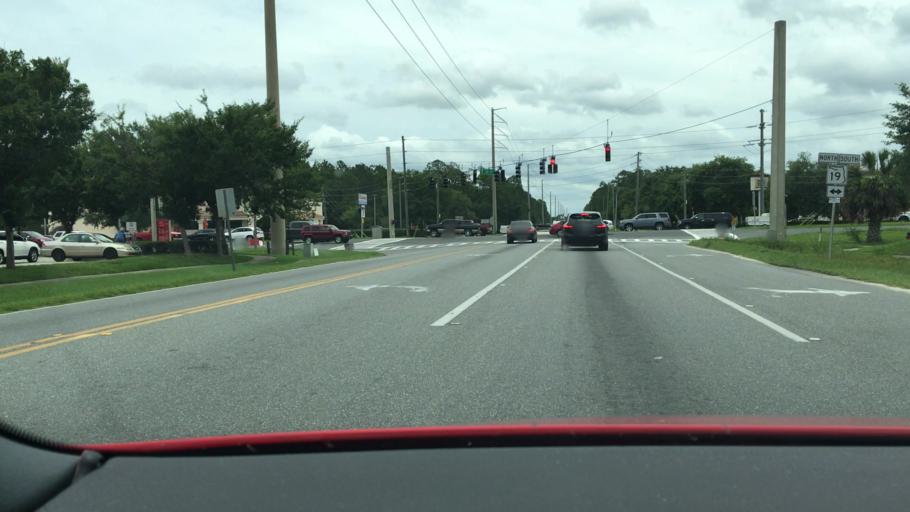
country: US
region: Florida
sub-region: Lake County
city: Eustis
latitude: 28.8753
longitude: -81.6887
